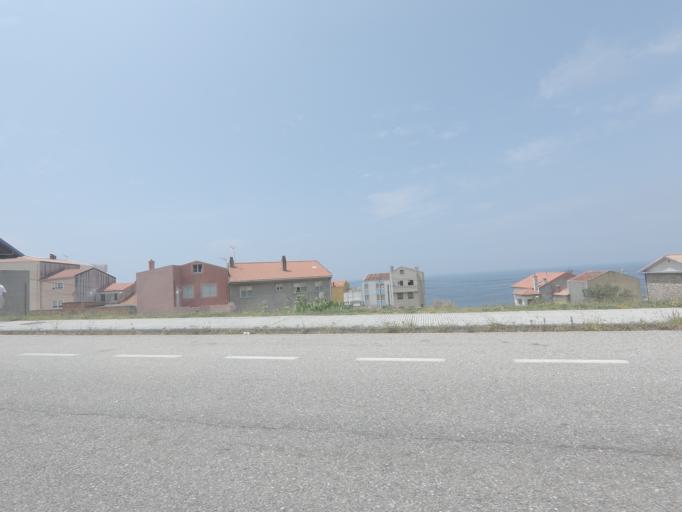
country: ES
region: Galicia
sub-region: Provincia de Pontevedra
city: A Guarda
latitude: 41.8938
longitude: -8.8765
